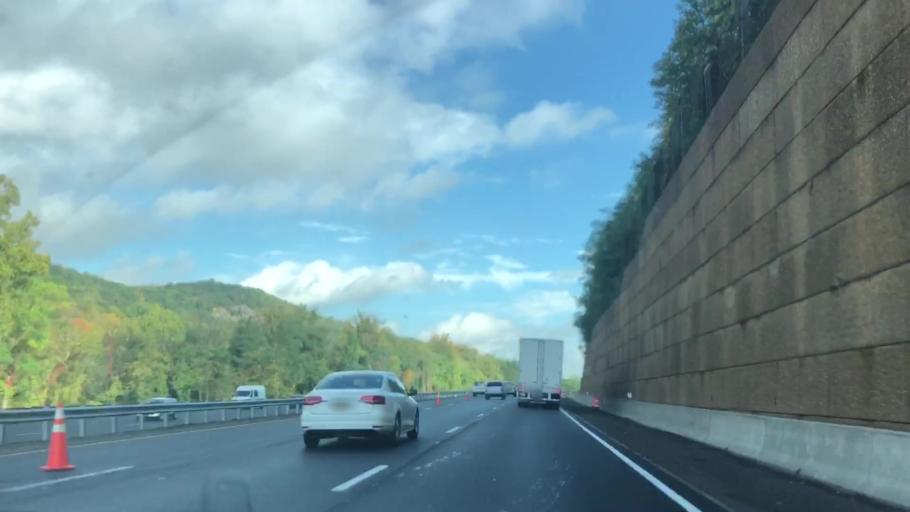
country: US
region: New York
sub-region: Orange County
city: Harriman
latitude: 41.2687
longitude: -74.1541
